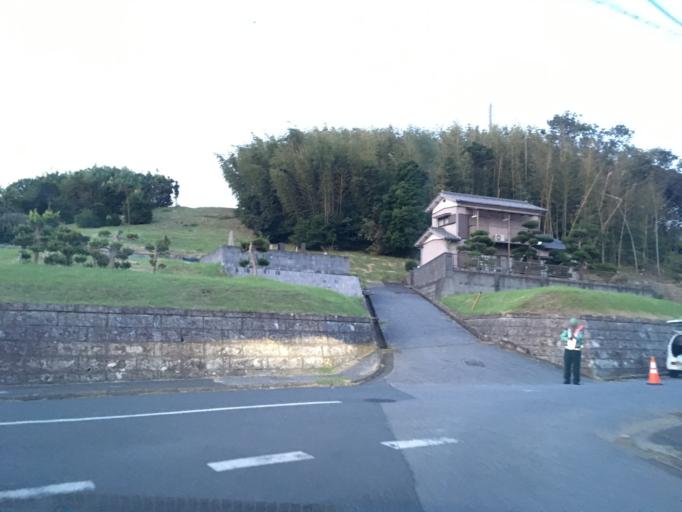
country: JP
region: Chiba
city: Kimitsu
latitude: 35.3439
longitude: 139.9140
